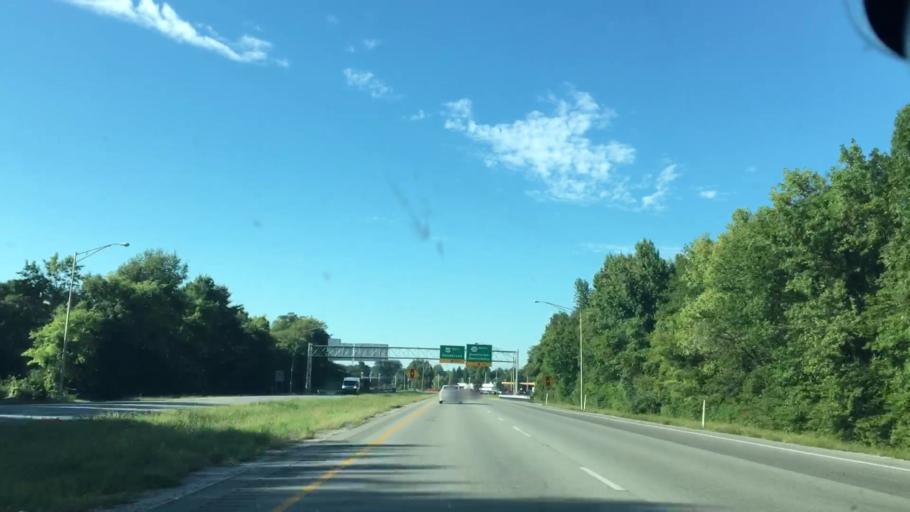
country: US
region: Kentucky
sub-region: Daviess County
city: Owensboro
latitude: 37.7713
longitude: -87.1651
